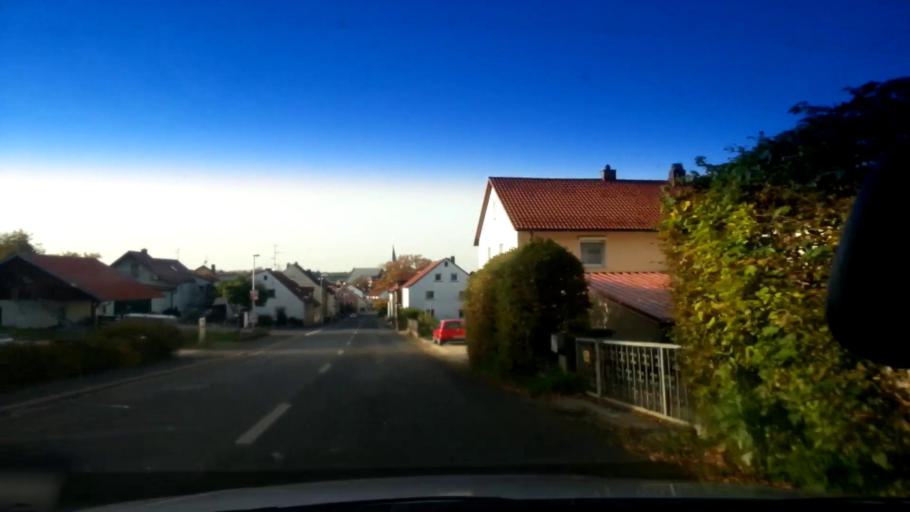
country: DE
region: Bavaria
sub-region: Upper Franconia
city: Schesslitz
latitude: 49.9728
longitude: 11.0405
